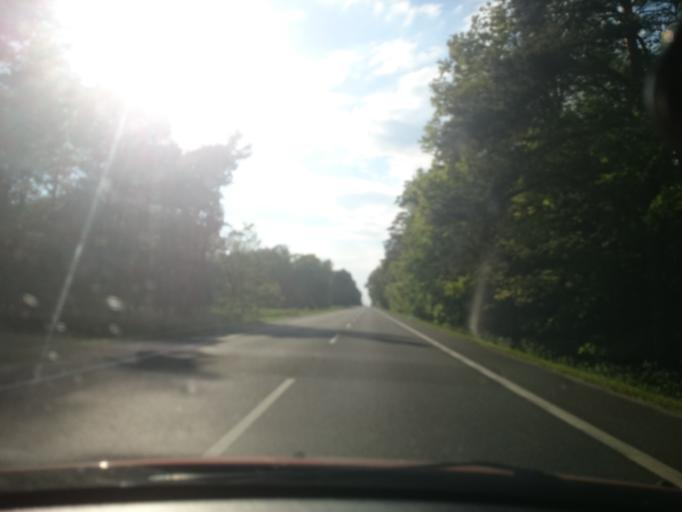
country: PL
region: Silesian Voivodeship
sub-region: Powiat gliwicki
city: Toszek
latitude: 50.4791
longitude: 18.4454
